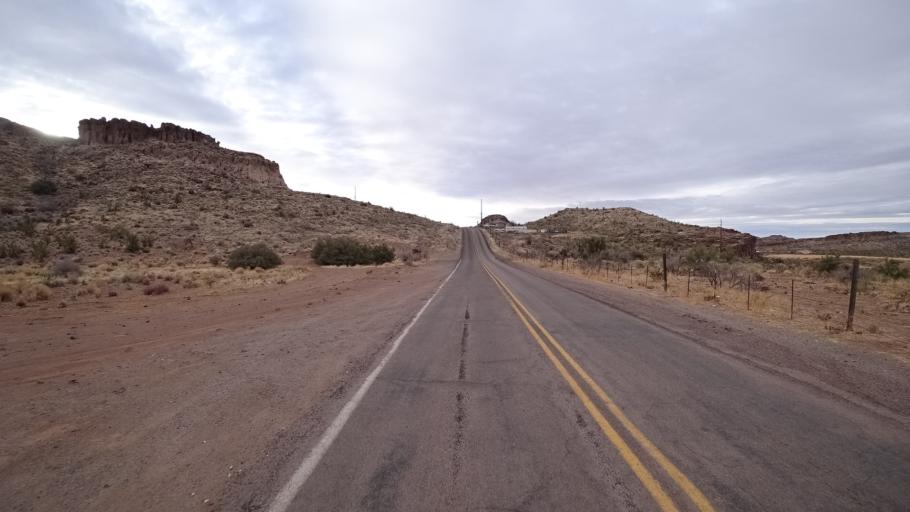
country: US
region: Arizona
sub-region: Mohave County
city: Kingman
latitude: 35.2194
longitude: -114.0656
